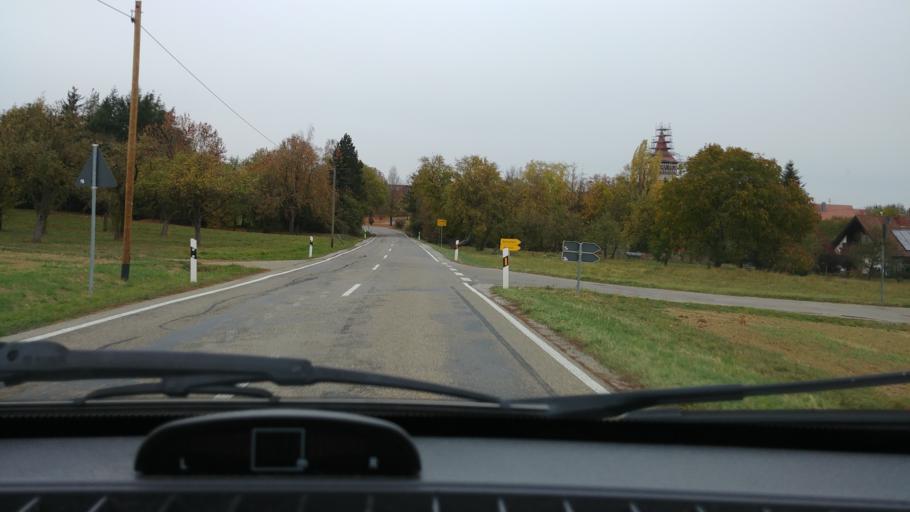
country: DE
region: Bavaria
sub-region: Regierungsbezirk Mittelfranken
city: Insingen
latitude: 49.3447
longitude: 10.0921
